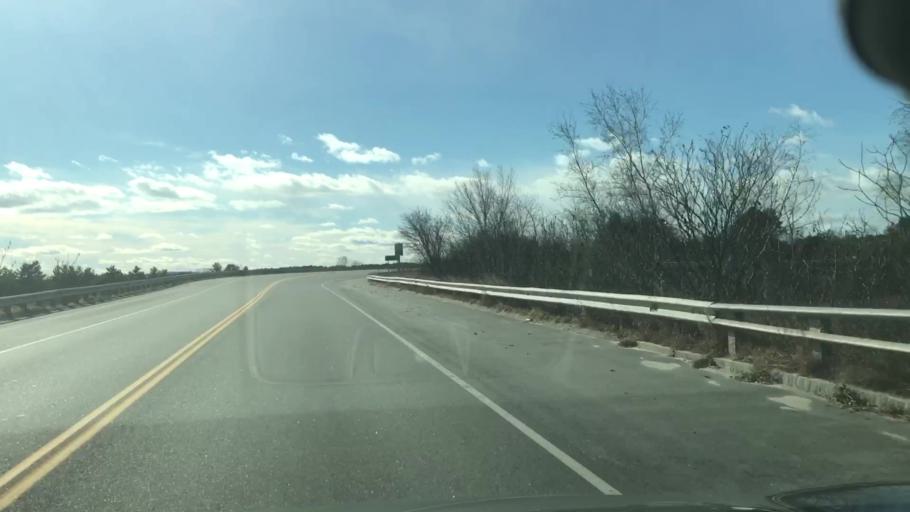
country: US
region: New Hampshire
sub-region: Merrimack County
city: Chichester
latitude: 43.2340
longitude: -71.4672
